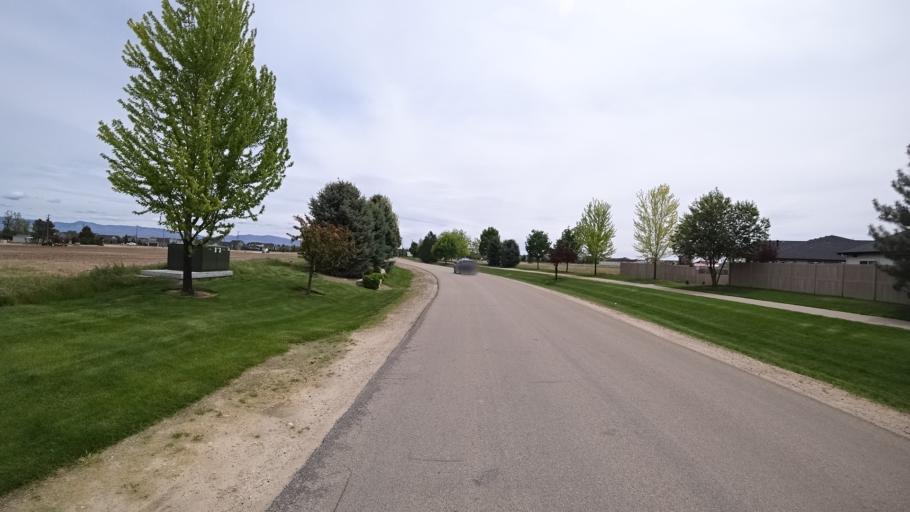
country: US
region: Idaho
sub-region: Ada County
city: Meridian
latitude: 43.5536
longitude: -116.3572
